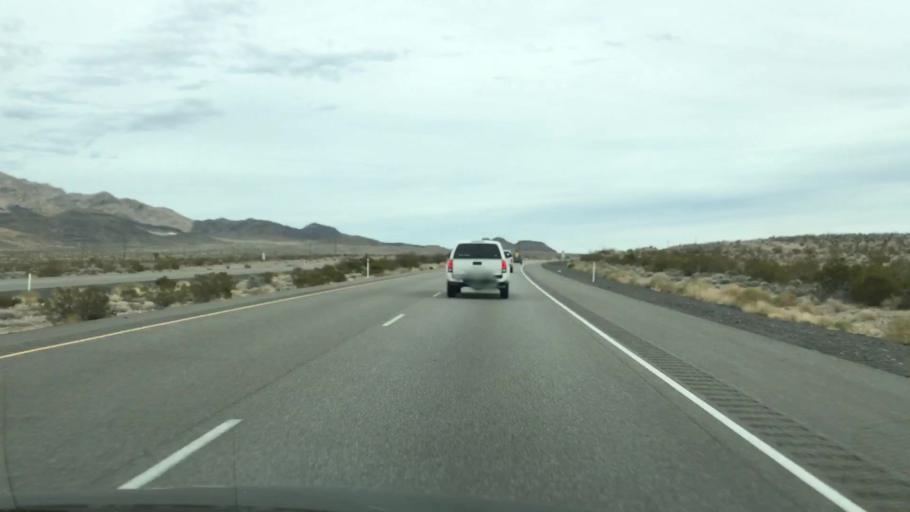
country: US
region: Nevada
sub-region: Nye County
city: Pahrump
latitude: 36.6010
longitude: -115.9810
